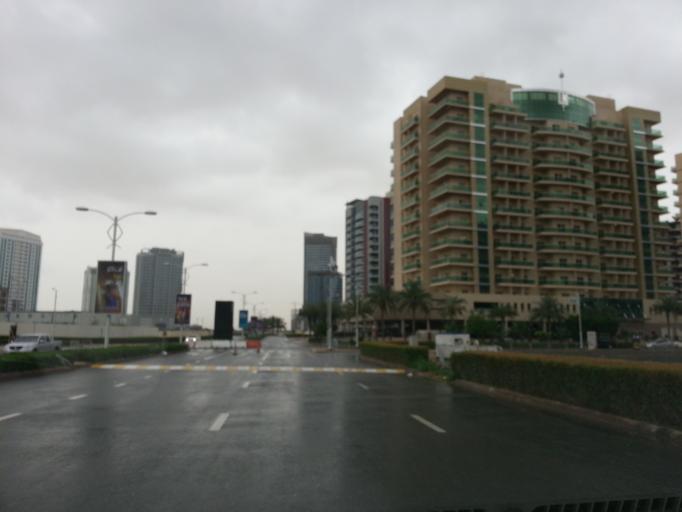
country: AE
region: Dubai
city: Dubai
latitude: 25.0451
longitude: 55.2169
